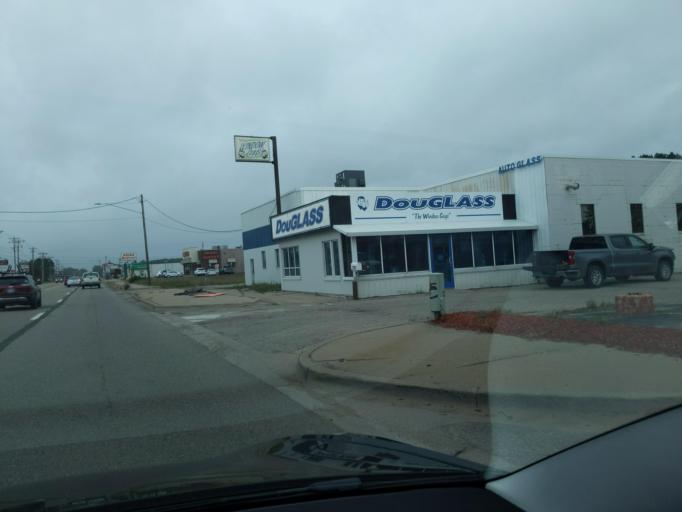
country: US
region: Michigan
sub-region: Wexford County
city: Cadillac
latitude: 44.2759
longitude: -85.4065
